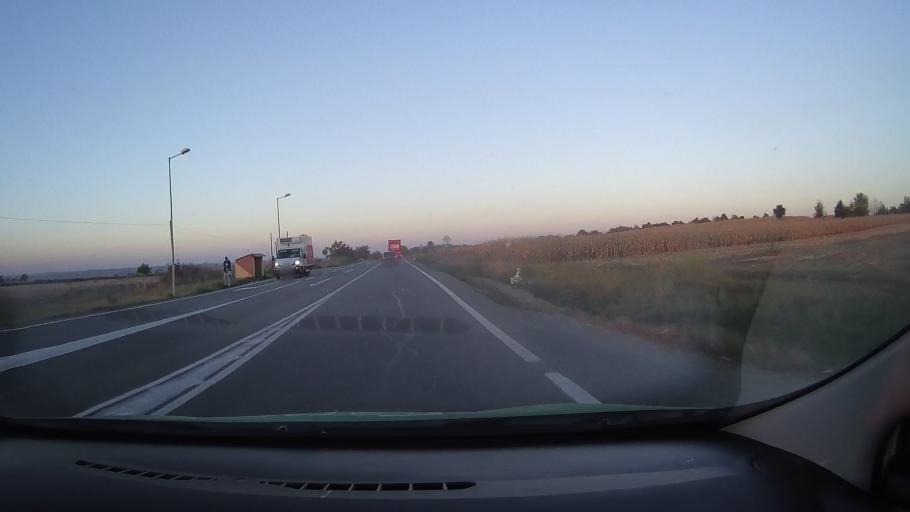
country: RO
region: Bihor
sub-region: Comuna Cherechiu
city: Cherechiu
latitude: 47.3759
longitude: 22.1373
